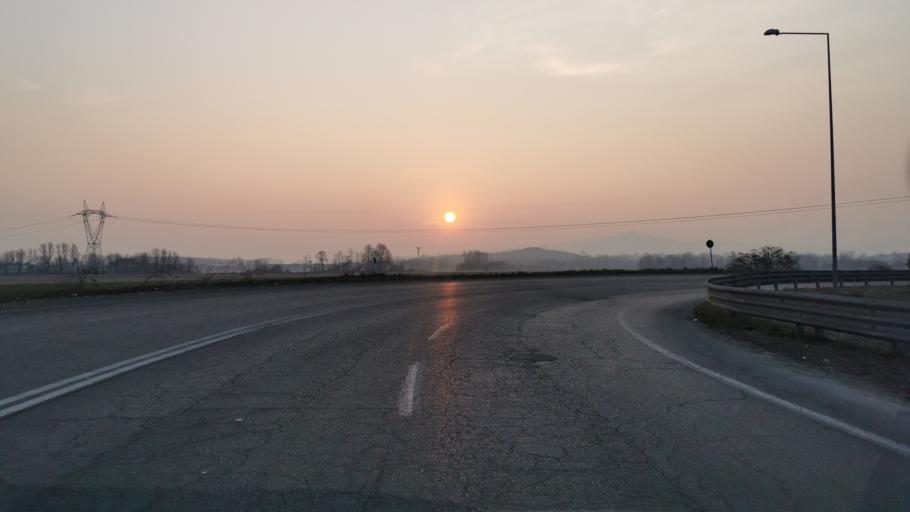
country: IT
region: Piedmont
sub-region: Provincia di Torino
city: Borgaro Torinese
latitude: 45.1315
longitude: 7.6580
